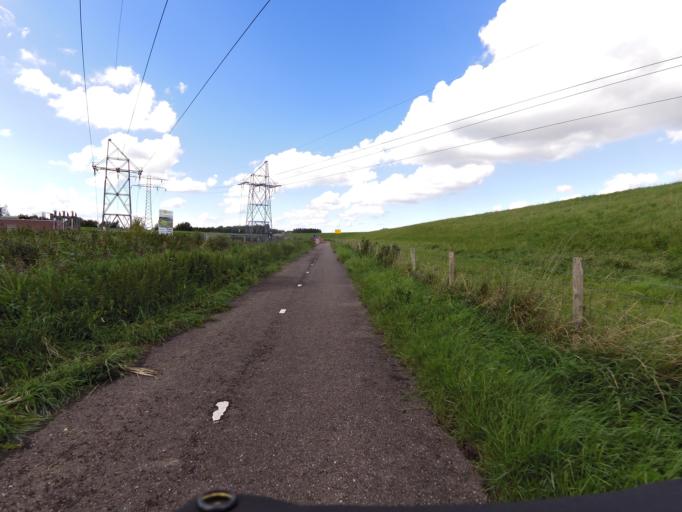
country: NL
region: North Brabant
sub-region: Gemeente Steenbergen
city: Dinteloord
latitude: 51.6993
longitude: 4.3339
